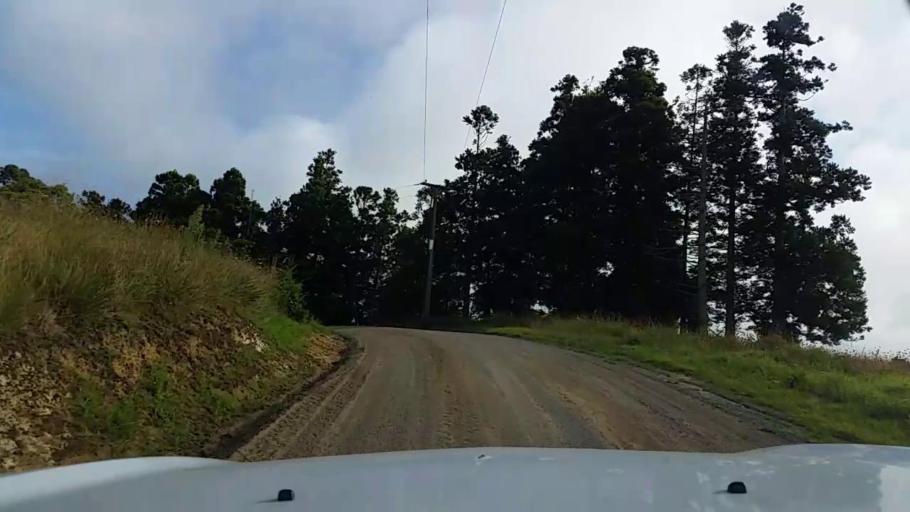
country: NZ
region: Northland
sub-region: Whangarei
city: Maungatapere
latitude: -35.6744
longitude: 174.1765
